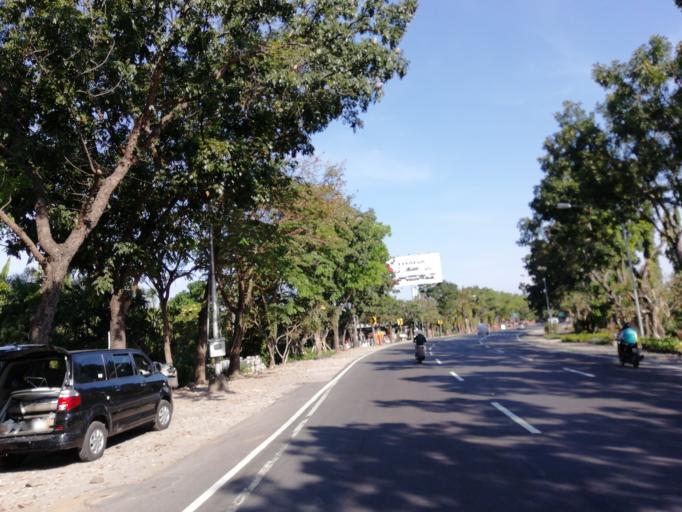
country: ID
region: Bali
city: Banjar Kertajiwa
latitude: -8.6461
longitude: 115.2571
